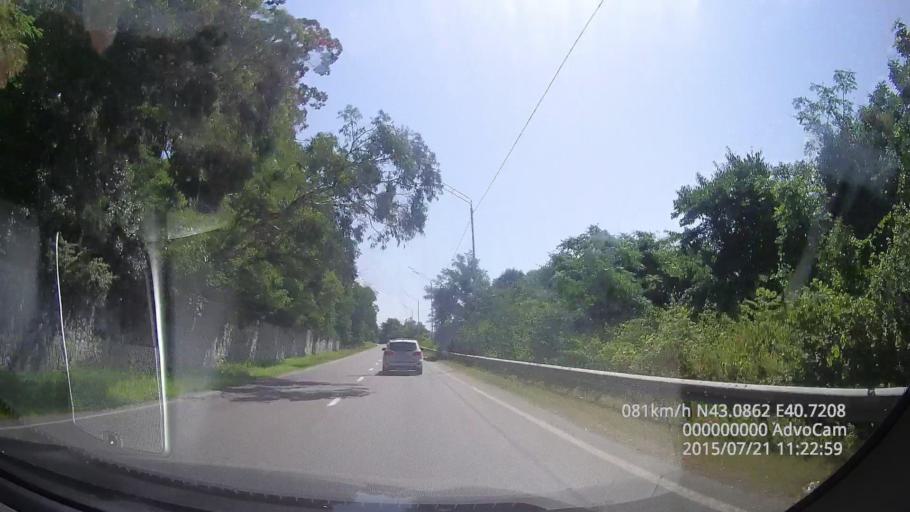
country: GE
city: P'rimorsk'oe
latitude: 43.0861
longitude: 40.7214
